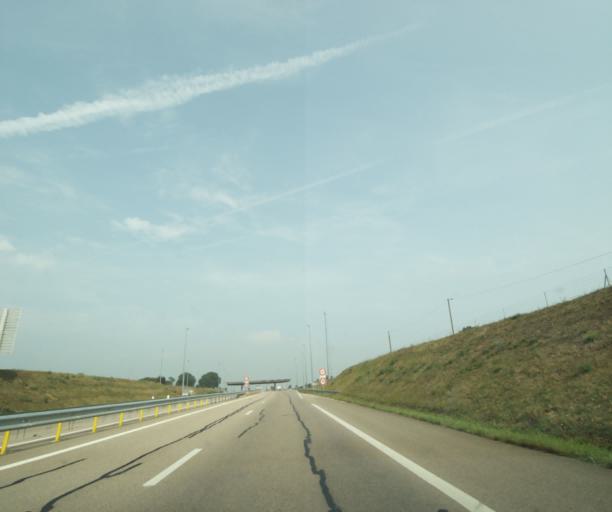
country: FR
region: Lower Normandy
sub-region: Departement de l'Orne
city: Courteilles
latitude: 48.8141
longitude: -0.1278
